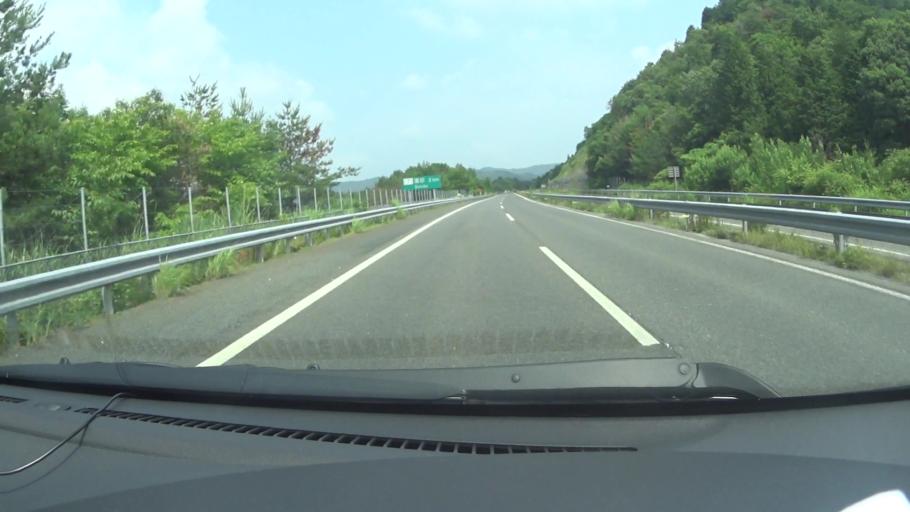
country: JP
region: Kyoto
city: Kameoka
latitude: 35.1039
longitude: 135.4876
